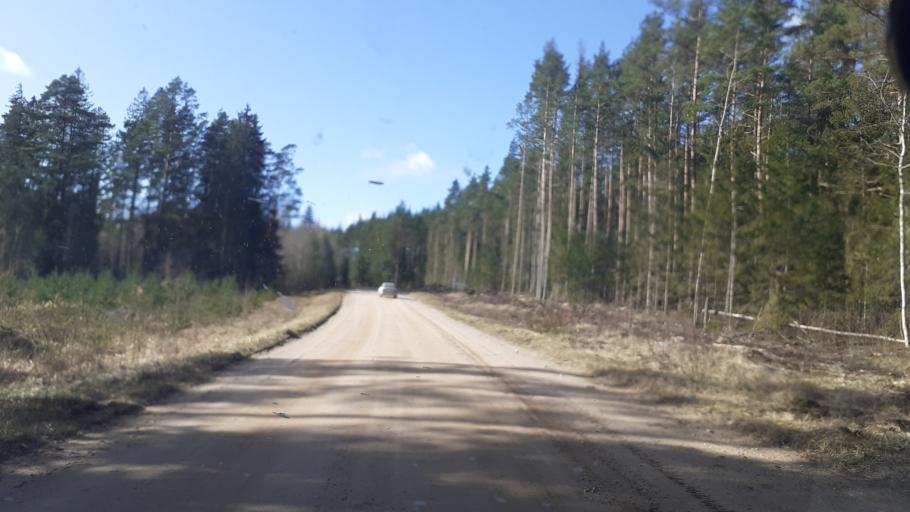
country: LV
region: Kuldigas Rajons
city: Kuldiga
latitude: 56.9127
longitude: 22.0895
